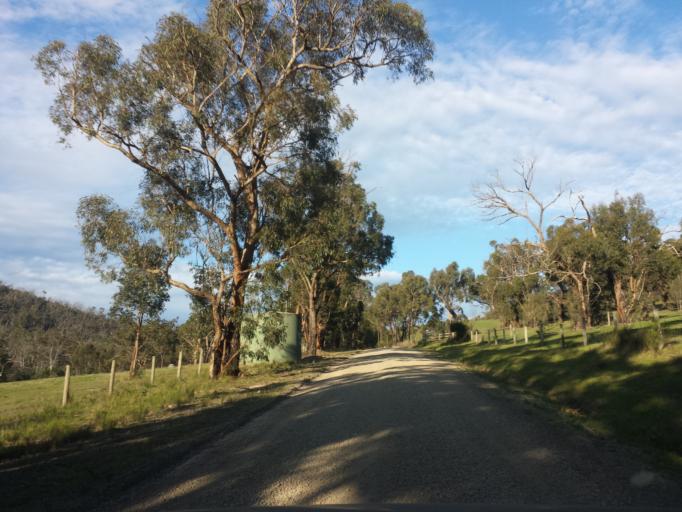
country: AU
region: Victoria
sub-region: Yarra Ranges
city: Yarra Glen
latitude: -37.5822
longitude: 145.3934
